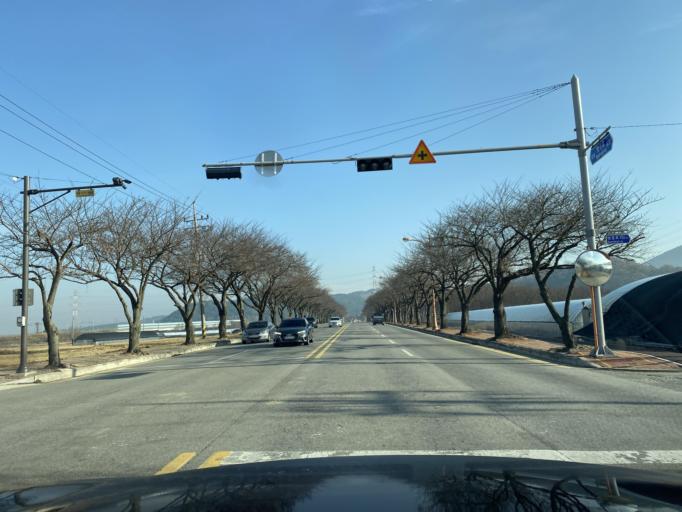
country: KR
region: Chungcheongnam-do
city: Yesan
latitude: 36.7303
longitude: 126.8576
